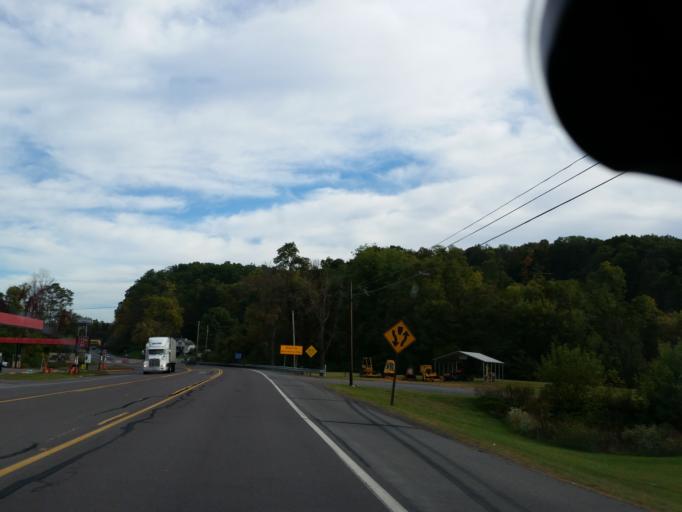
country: US
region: Pennsylvania
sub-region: Northumberland County
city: Dewart
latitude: 41.1022
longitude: -76.8935
